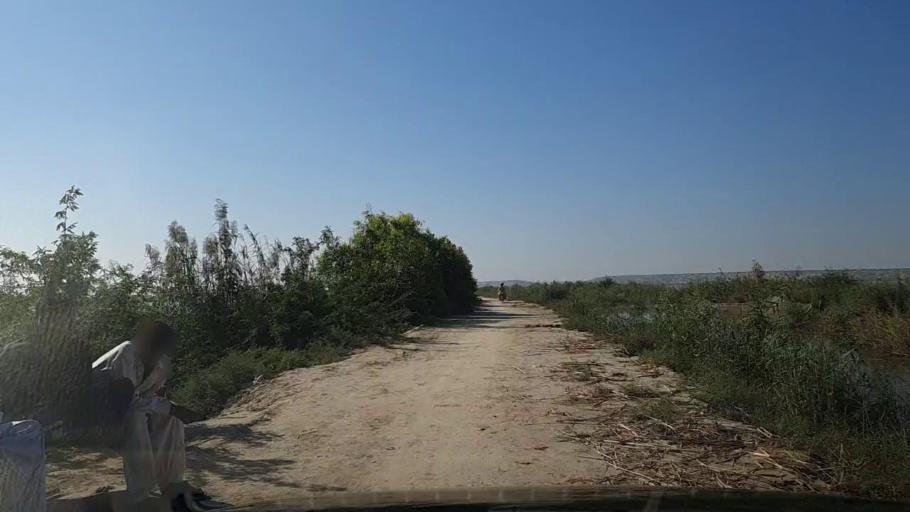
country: PK
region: Sindh
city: Thatta
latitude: 24.6973
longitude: 67.8968
